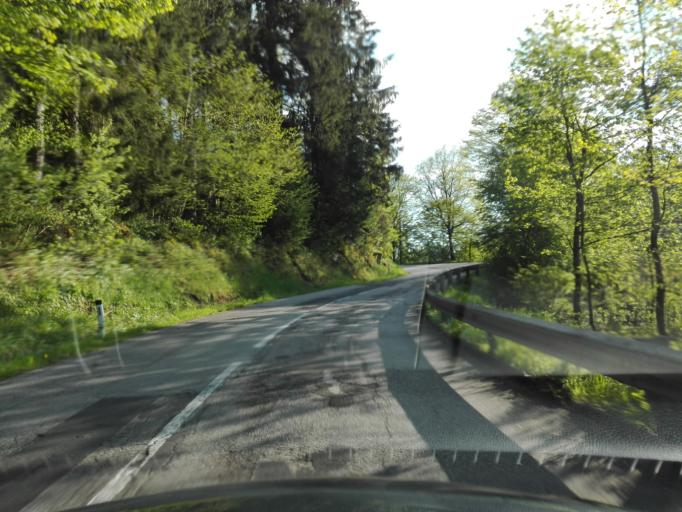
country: AT
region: Upper Austria
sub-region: Politischer Bezirk Rohrbach
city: Atzesberg
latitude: 48.4802
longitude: 13.9336
